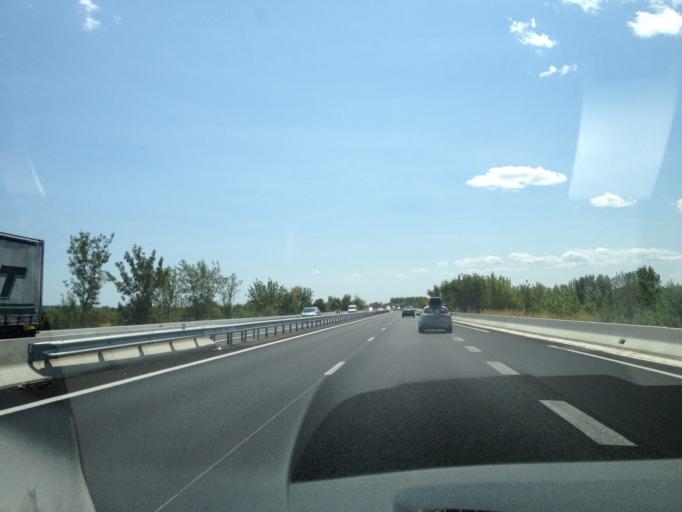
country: FR
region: Languedoc-Roussillon
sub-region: Departement de l'Herault
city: Pezenas
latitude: 43.4727
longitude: 3.4355
